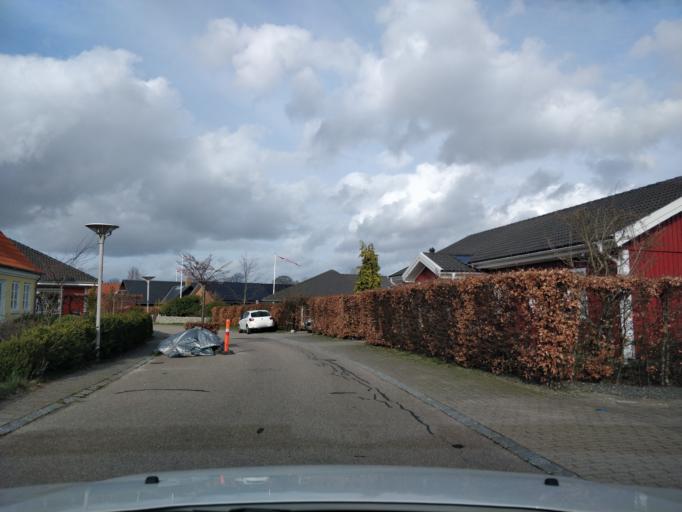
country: DK
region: Capital Region
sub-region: Hoje-Taastrup Kommune
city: Taastrup
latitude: 55.6482
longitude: 12.2522
